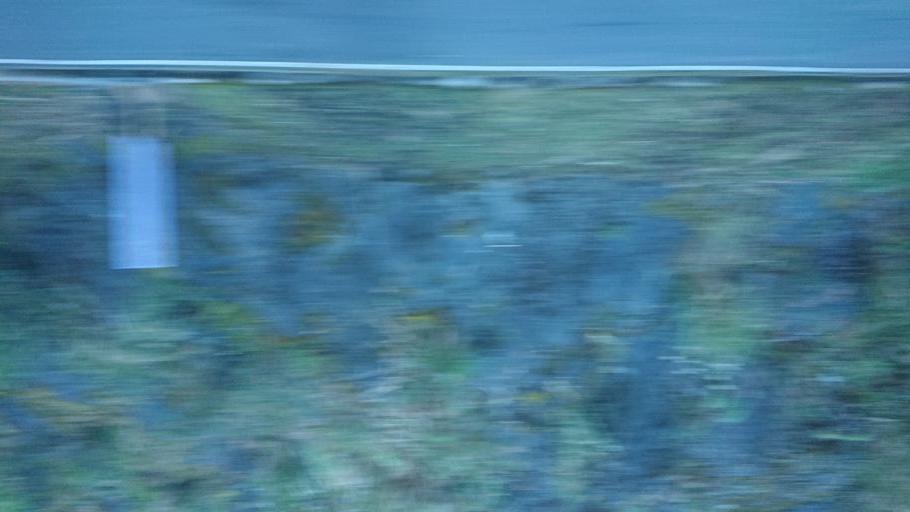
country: TW
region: Taiwan
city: Lugu
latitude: 23.4736
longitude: 120.8389
